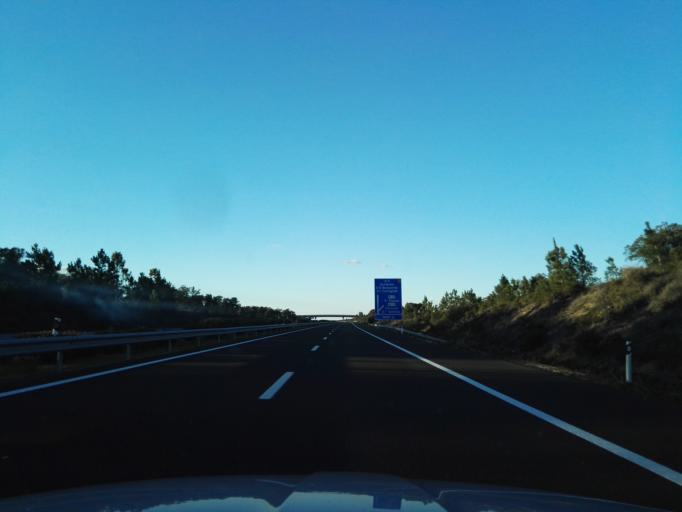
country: PT
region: Santarem
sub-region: Benavente
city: Poceirao
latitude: 38.8245
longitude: -8.7154
